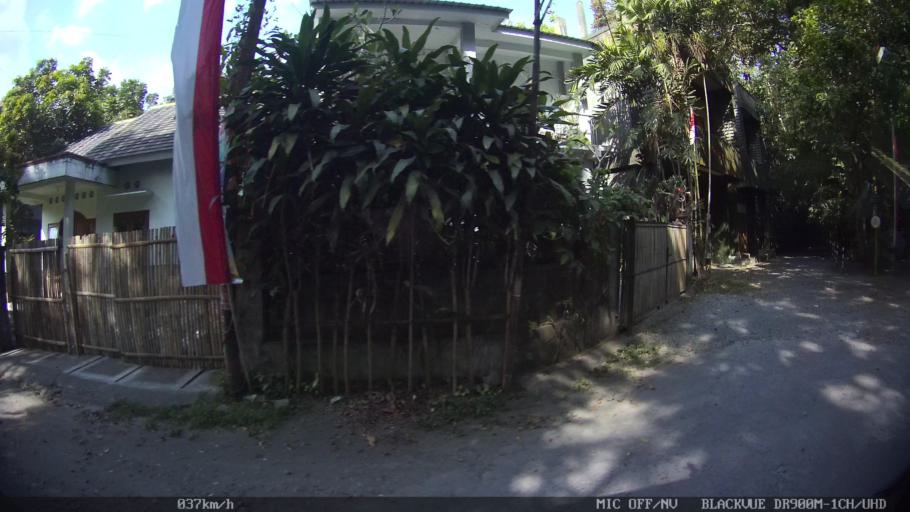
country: ID
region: Daerah Istimewa Yogyakarta
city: Kasihan
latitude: -7.8319
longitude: 110.3387
